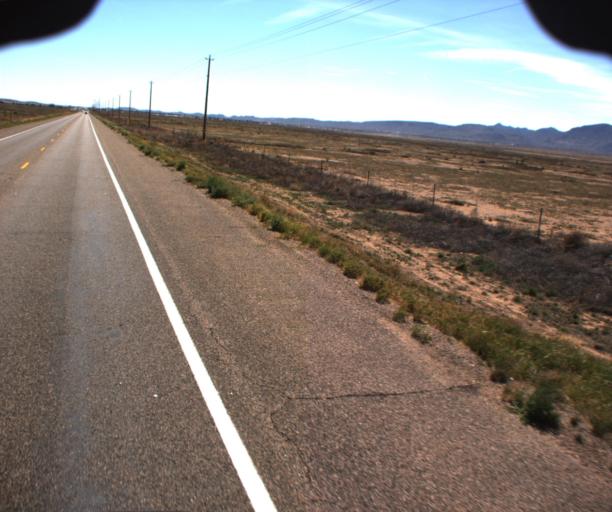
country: US
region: Arizona
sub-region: Mohave County
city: New Kingman-Butler
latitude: 35.2836
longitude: -113.9473
